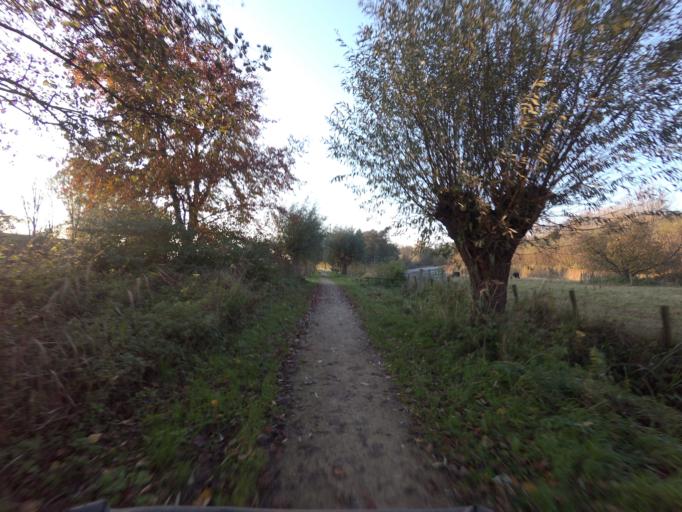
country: NL
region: North Brabant
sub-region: Gemeente Woudrichem
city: Woudrichem
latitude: 51.7881
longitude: 5.0253
